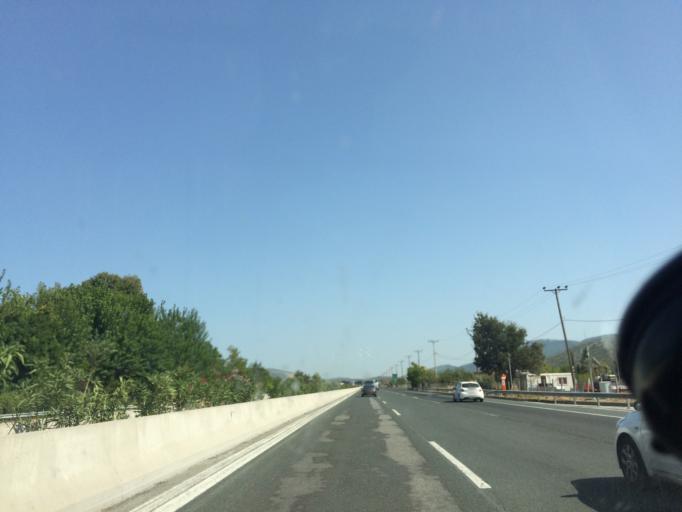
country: GR
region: Attica
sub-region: Nomarchia Anatolikis Attikis
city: Avlonas
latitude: 38.2614
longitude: 23.7306
